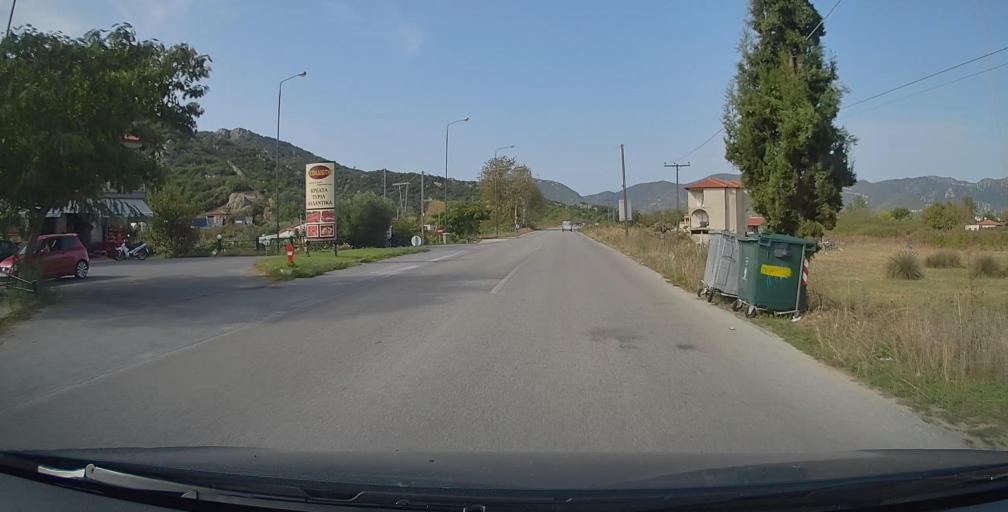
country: GR
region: Central Macedonia
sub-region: Nomos Chalkidikis
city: Sykia
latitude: 40.0326
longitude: 23.9768
